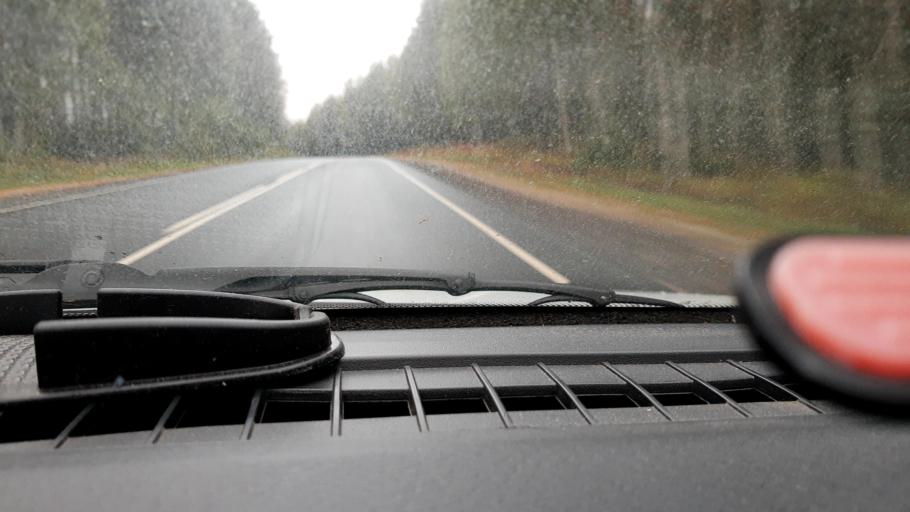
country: RU
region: Nizjnij Novgorod
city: Semenov
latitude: 56.7251
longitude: 44.2860
